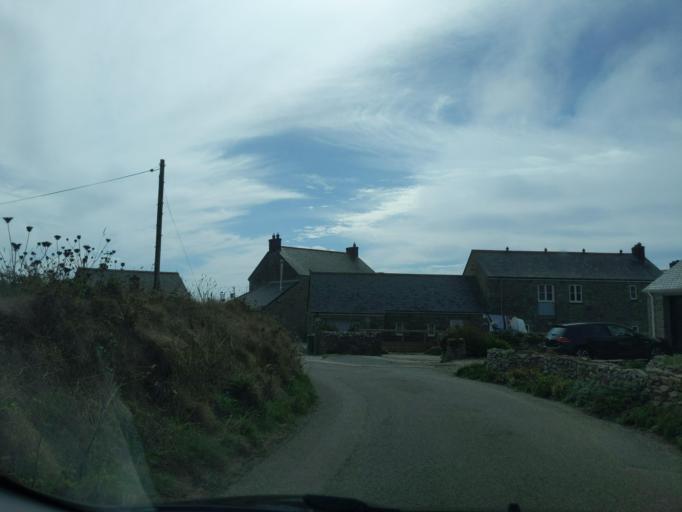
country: GB
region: England
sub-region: Cornwall
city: Germoe
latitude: 50.0975
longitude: -5.3660
